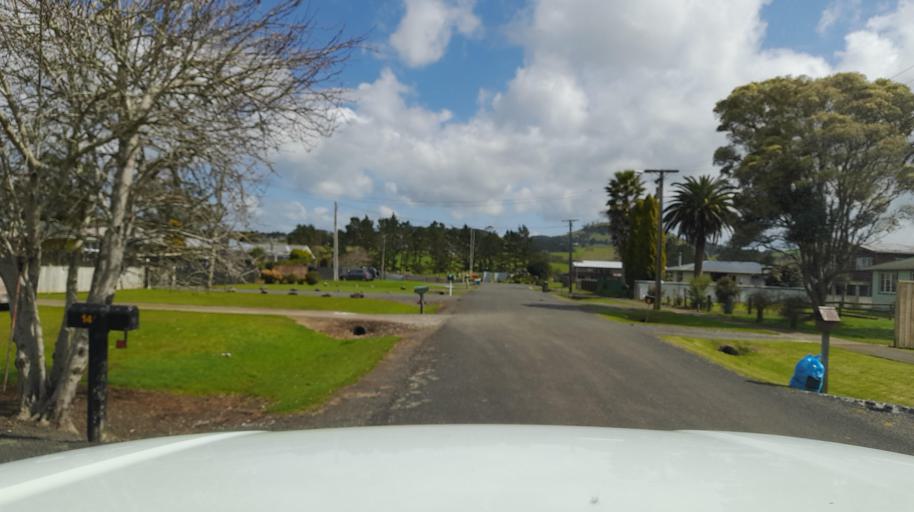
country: NZ
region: Northland
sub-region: Far North District
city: Waimate North
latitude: -35.3533
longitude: 173.8824
